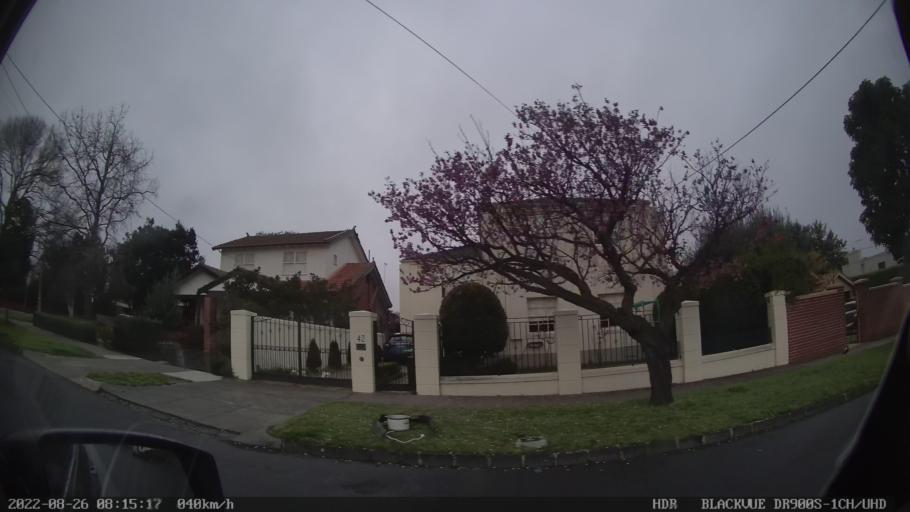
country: AU
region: Victoria
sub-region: Glen Eira
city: Elsternwick
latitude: -37.8935
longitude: 145.0086
